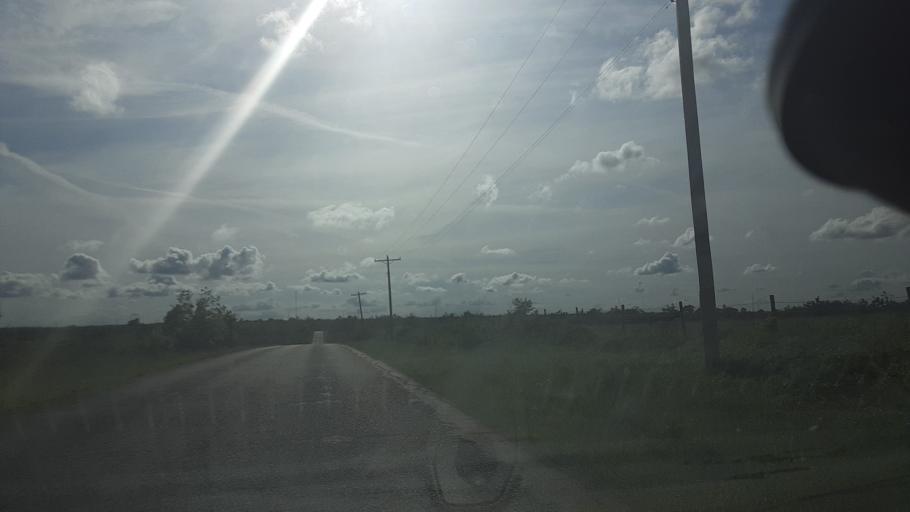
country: US
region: Oklahoma
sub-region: Logan County
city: Guthrie
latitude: 36.0578
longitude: -97.3994
